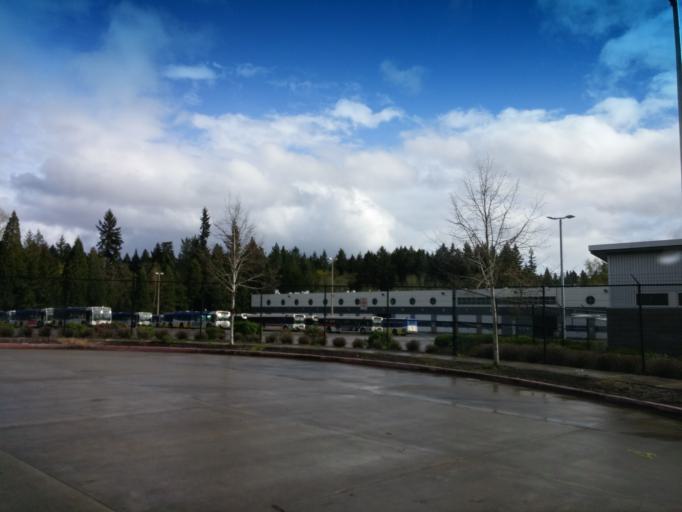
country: US
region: Oregon
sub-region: Washington County
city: Aloha
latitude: 45.5040
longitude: -122.8448
